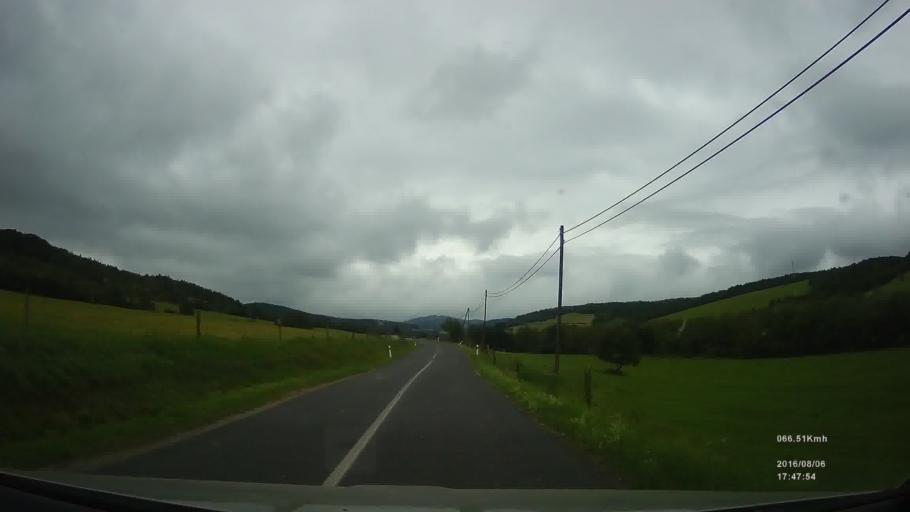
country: SK
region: Presovsky
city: Svidnik
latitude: 49.3722
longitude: 21.5755
